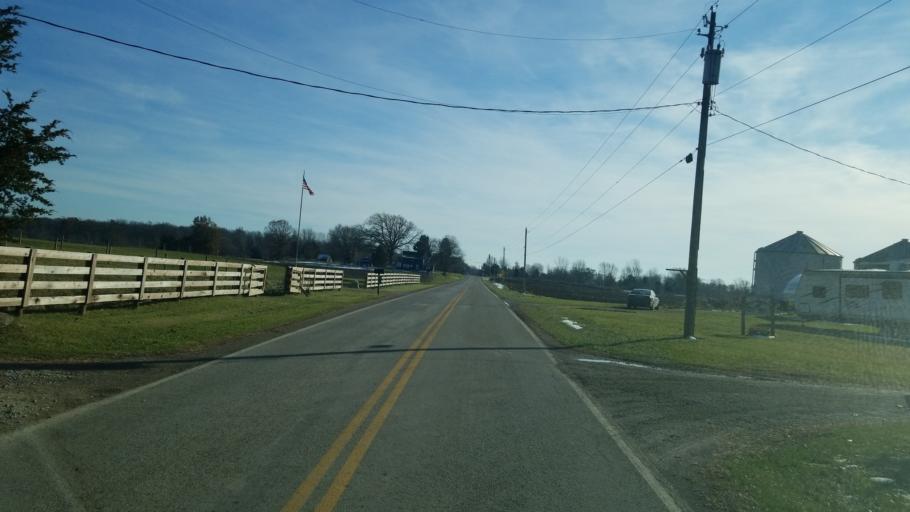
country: US
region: Ohio
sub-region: Lorain County
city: Camden
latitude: 41.1883
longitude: -82.3557
